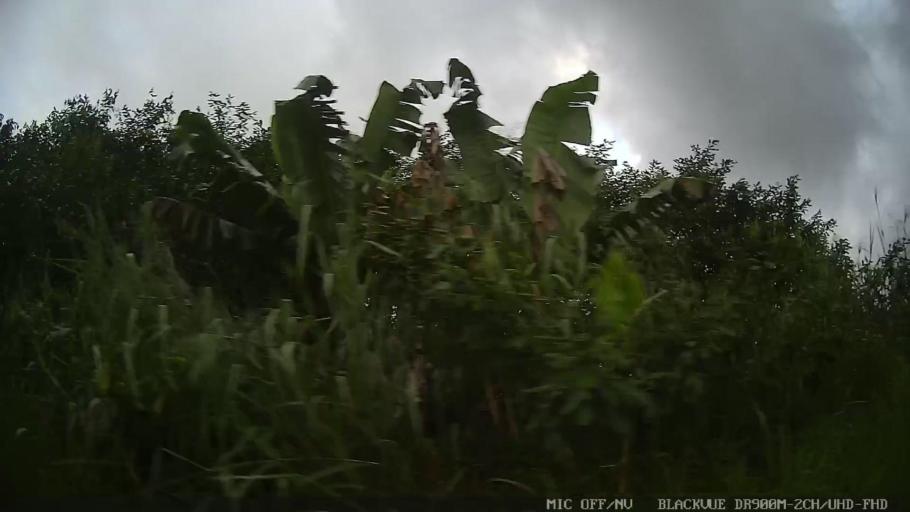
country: BR
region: Sao Paulo
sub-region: Itanhaem
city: Itanhaem
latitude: -24.0936
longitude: -46.7985
